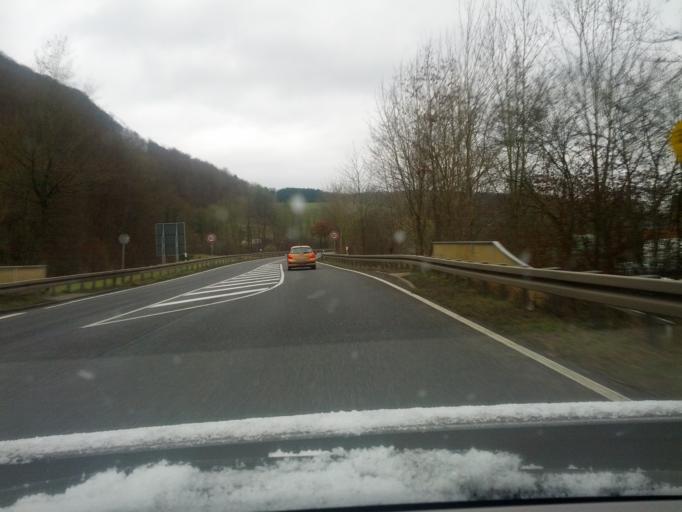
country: DE
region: Hesse
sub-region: Regierungsbezirk Kassel
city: Sontra
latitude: 51.0656
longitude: 9.9985
